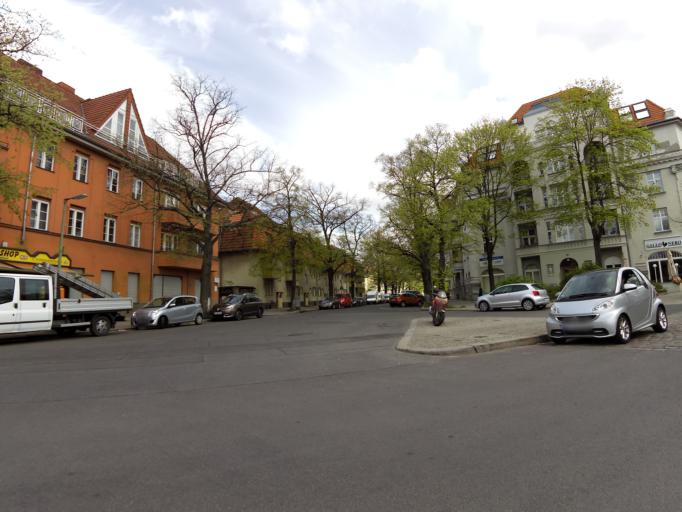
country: DE
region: Berlin
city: Britz
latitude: 52.4549
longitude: 13.4443
